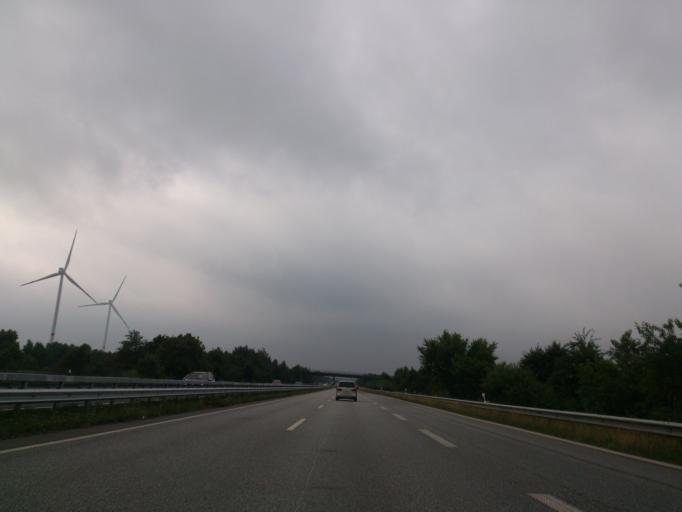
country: DE
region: Schleswig-Holstein
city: Tensbuttel-Rost
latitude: 54.1134
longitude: 9.2607
